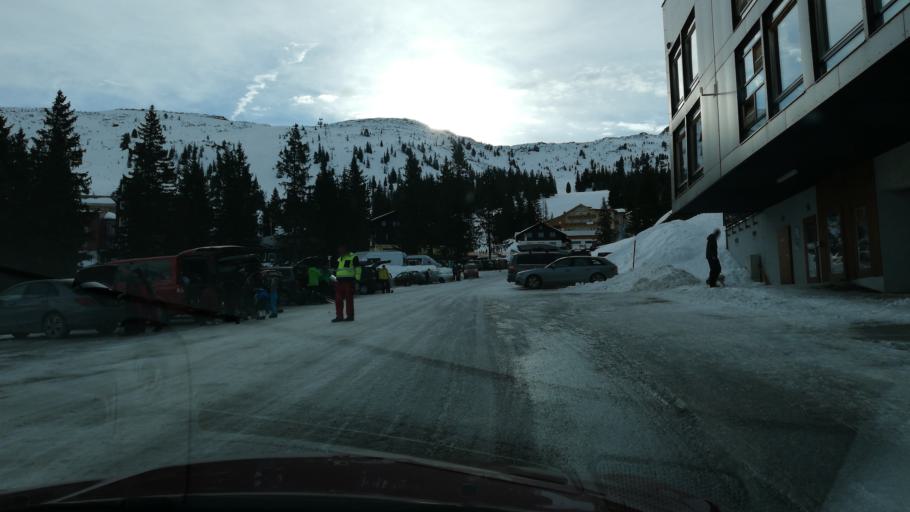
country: AT
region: Styria
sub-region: Politischer Bezirk Liezen
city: Donnersbach
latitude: 47.4052
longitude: 14.1978
